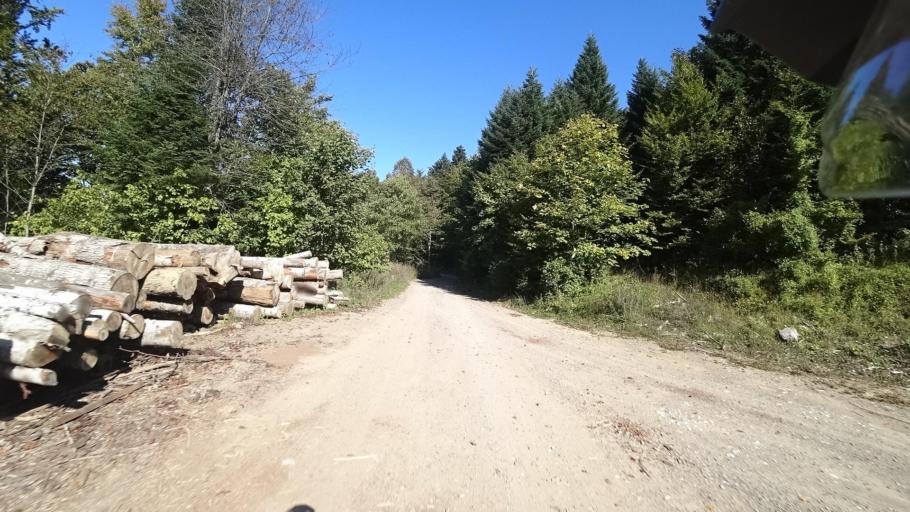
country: HR
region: Karlovacka
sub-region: Grad Ogulin
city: Ogulin
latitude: 45.2038
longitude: 15.1548
